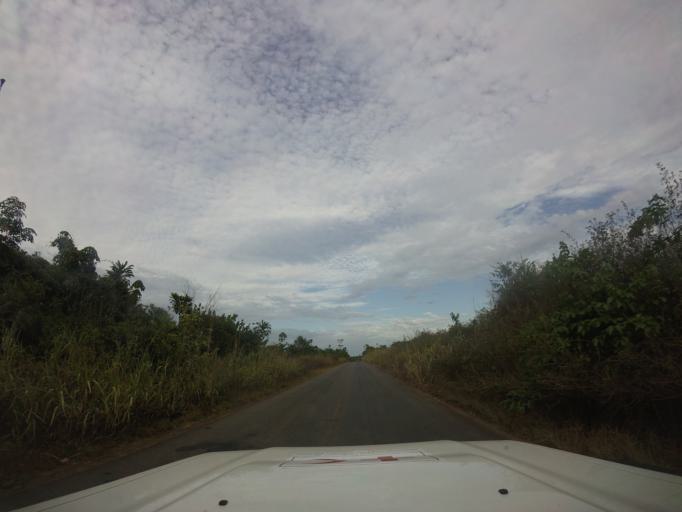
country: LR
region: Bomi
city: Tubmanburg
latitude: 6.7125
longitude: -10.9452
